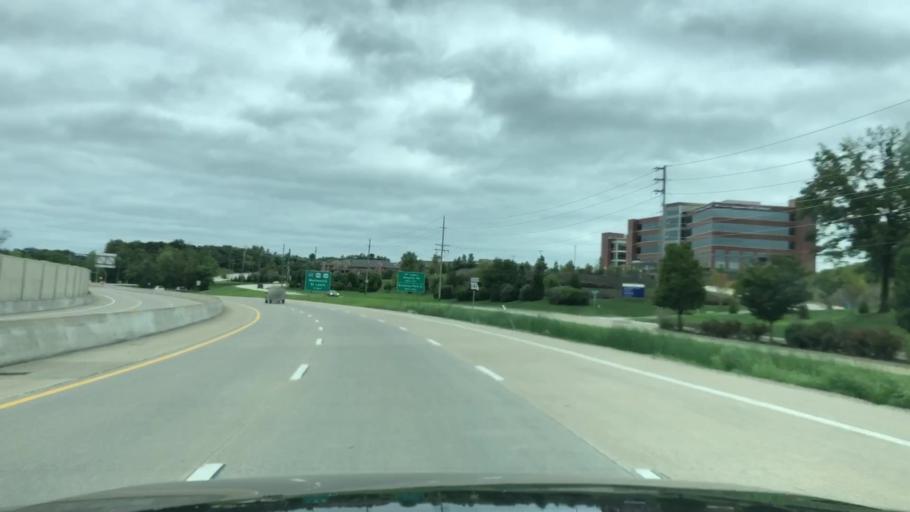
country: US
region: Missouri
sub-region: Saint Louis County
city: Manchester
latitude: 38.6575
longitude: -90.5064
